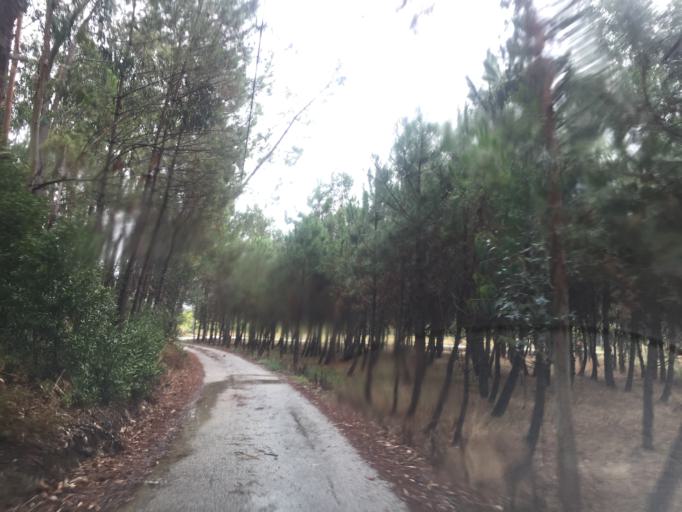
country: PT
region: Coimbra
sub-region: Figueira da Foz
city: Lavos
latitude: 40.0667
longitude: -8.7839
